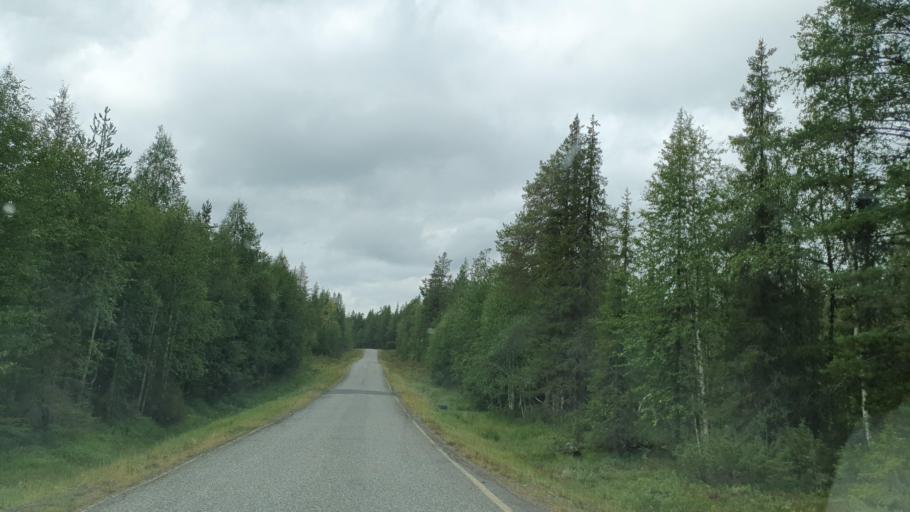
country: FI
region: Lapland
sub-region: Tunturi-Lappi
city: Kittilae
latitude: 67.7400
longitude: 24.2954
